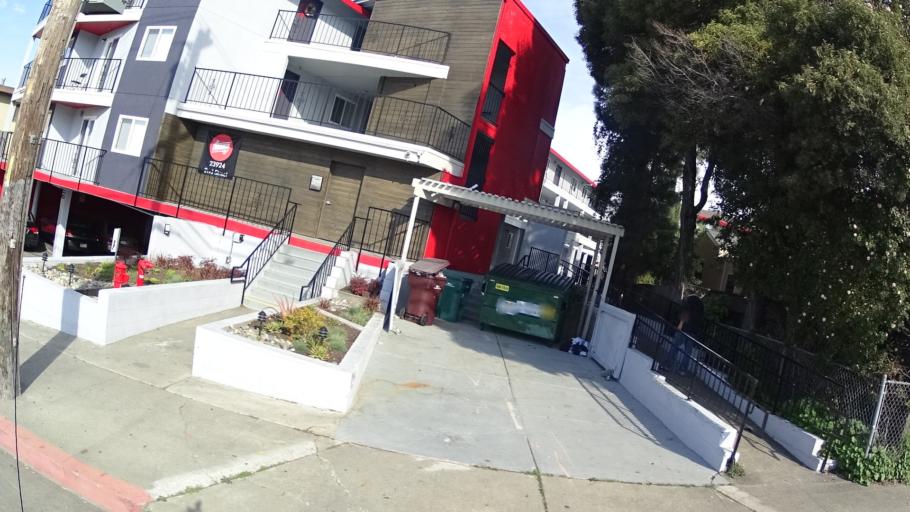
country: US
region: California
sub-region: Alameda County
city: Hayward
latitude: 37.6715
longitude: -122.0750
